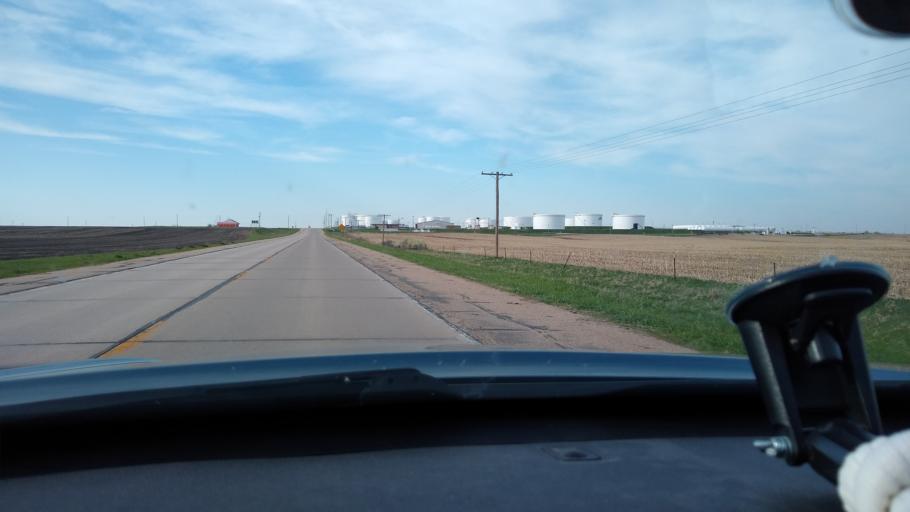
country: US
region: Nebraska
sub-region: Fillmore County
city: Geneva
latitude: 40.5453
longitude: -97.5958
